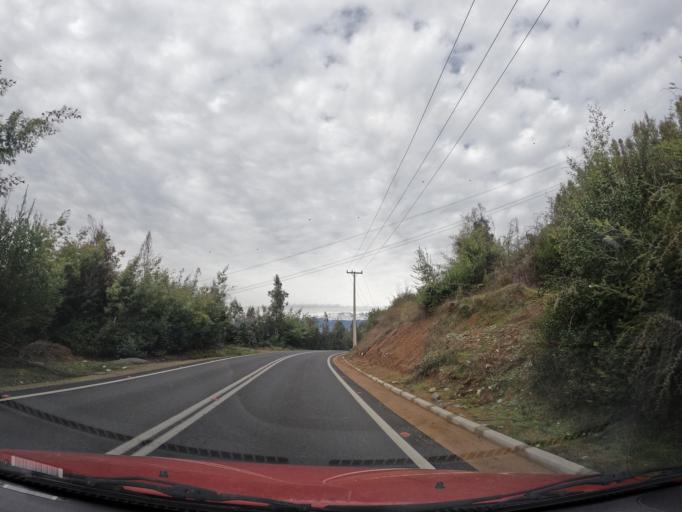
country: CL
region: Maule
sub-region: Provincia de Linares
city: Linares
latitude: -35.9240
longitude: -71.4465
